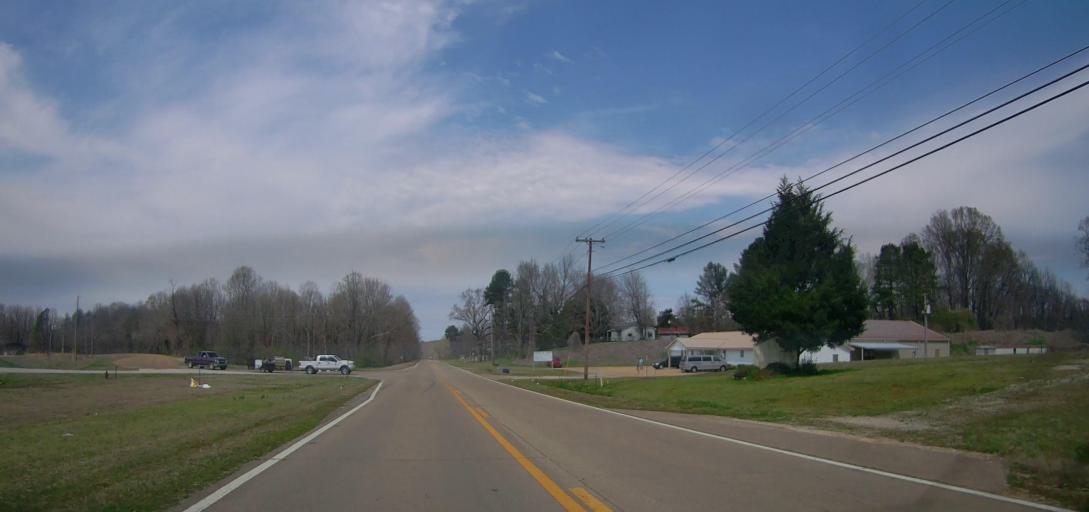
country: US
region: Mississippi
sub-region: Union County
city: New Albany
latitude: 34.4584
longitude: -88.9770
